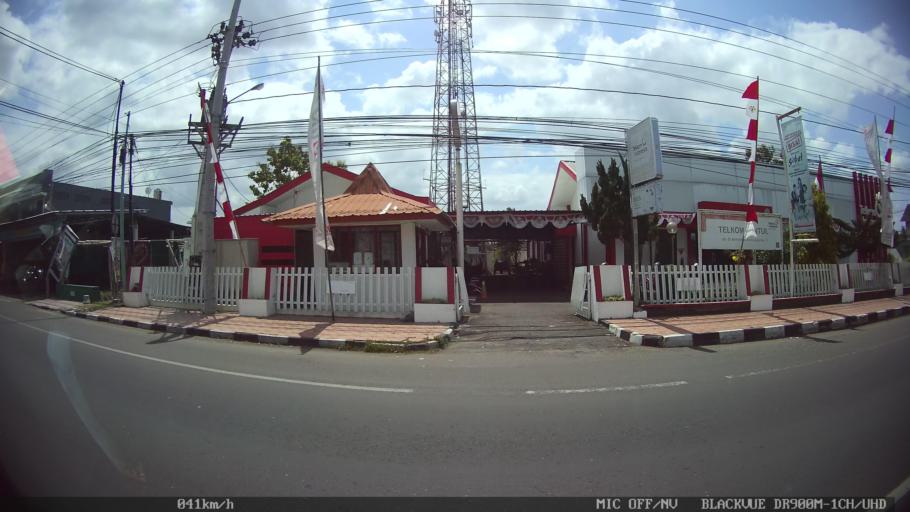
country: ID
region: Daerah Istimewa Yogyakarta
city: Bantul
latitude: -7.8928
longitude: 110.3355
